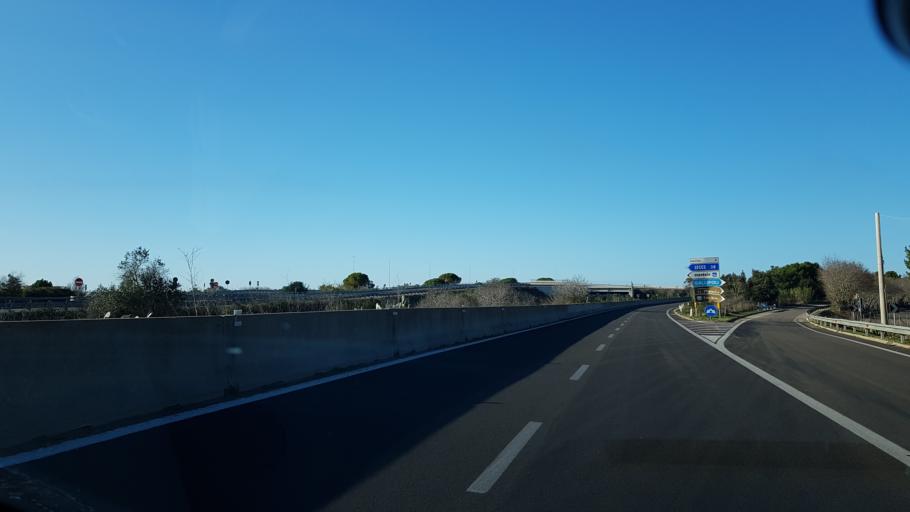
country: IT
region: Apulia
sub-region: Provincia di Lecce
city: Gallipoli
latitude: 40.0392
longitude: 18.0221
